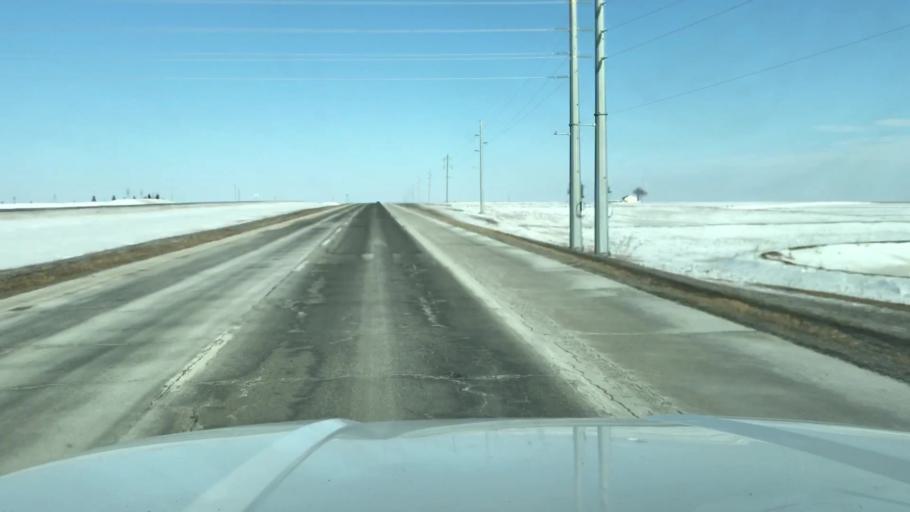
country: US
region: Missouri
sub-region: Nodaway County
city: Maryville
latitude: 40.2257
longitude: -94.8678
